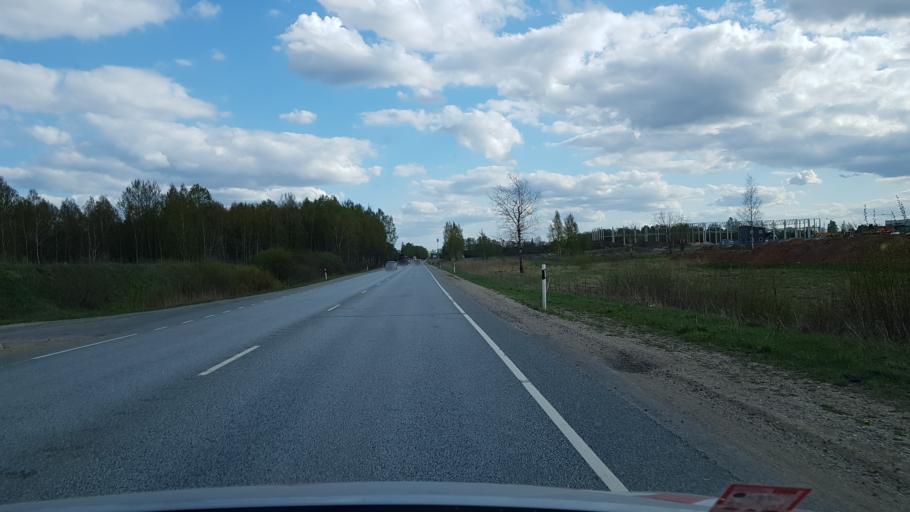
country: EE
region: Tartu
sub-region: UElenurme vald
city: Ulenurme
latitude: 58.3055
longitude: 26.7182
